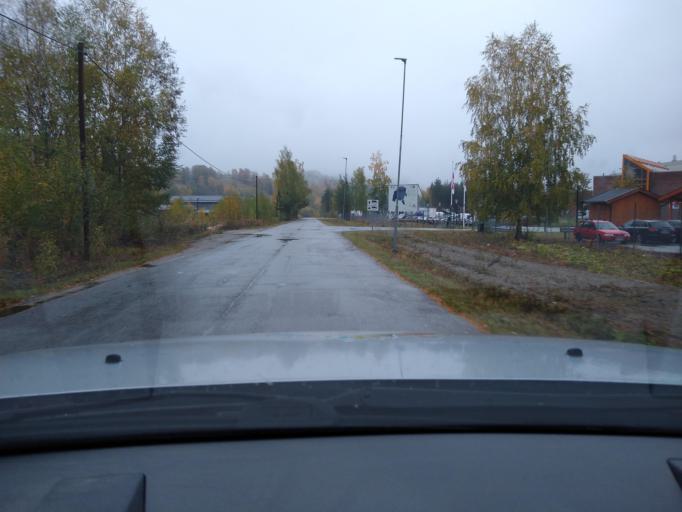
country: NO
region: Oppland
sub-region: Ringebu
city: Ringebu
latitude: 61.5477
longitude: 10.0633
